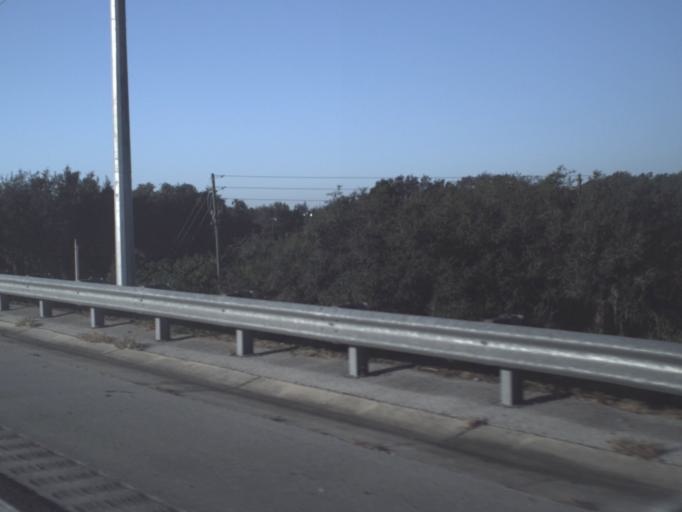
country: US
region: Florida
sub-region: Polk County
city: Citrus Ridge
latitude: 28.3336
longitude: -81.6155
